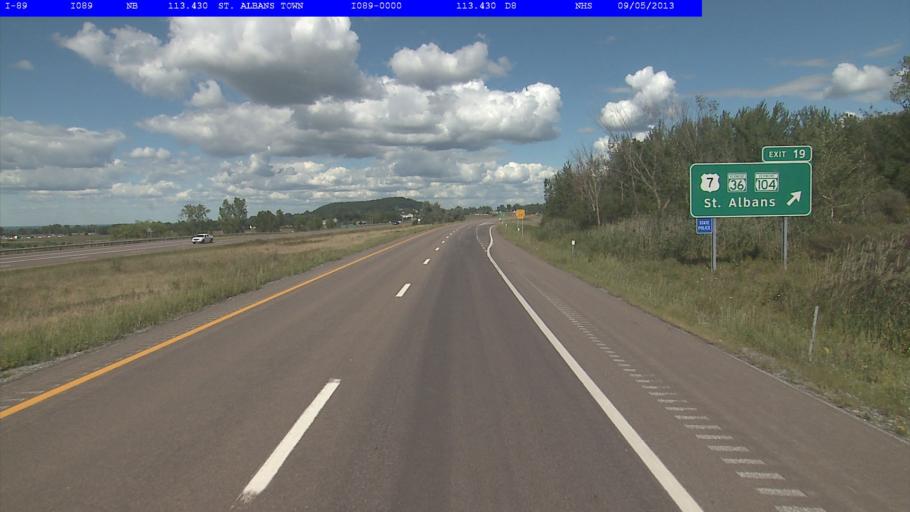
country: US
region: Vermont
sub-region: Franklin County
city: Saint Albans
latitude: 44.7904
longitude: -73.0712
